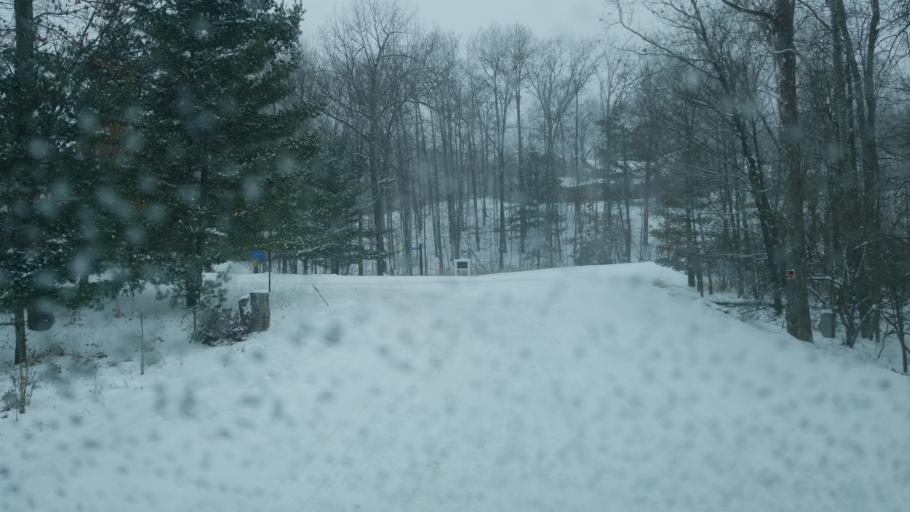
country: US
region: Michigan
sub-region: Mecosta County
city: Canadian Lakes
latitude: 43.6048
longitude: -85.3041
